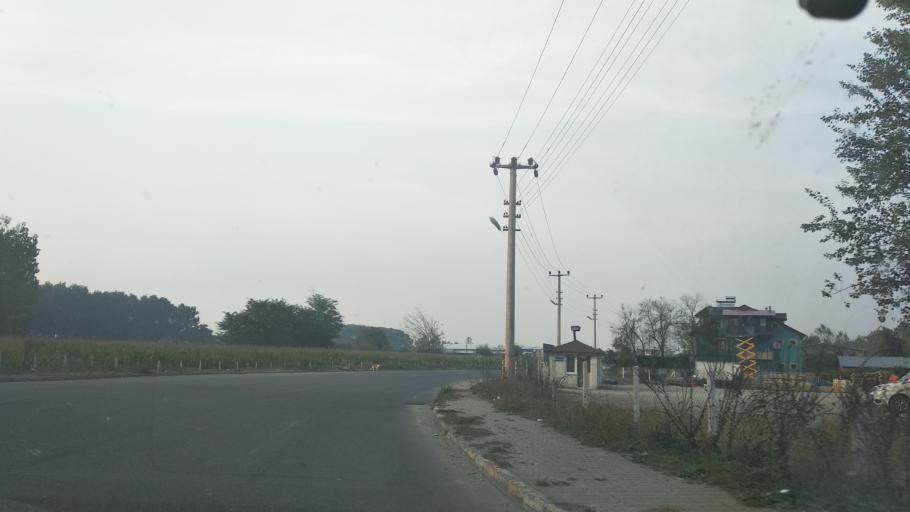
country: TR
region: Duzce
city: Duzce
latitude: 40.8111
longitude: 31.1778
